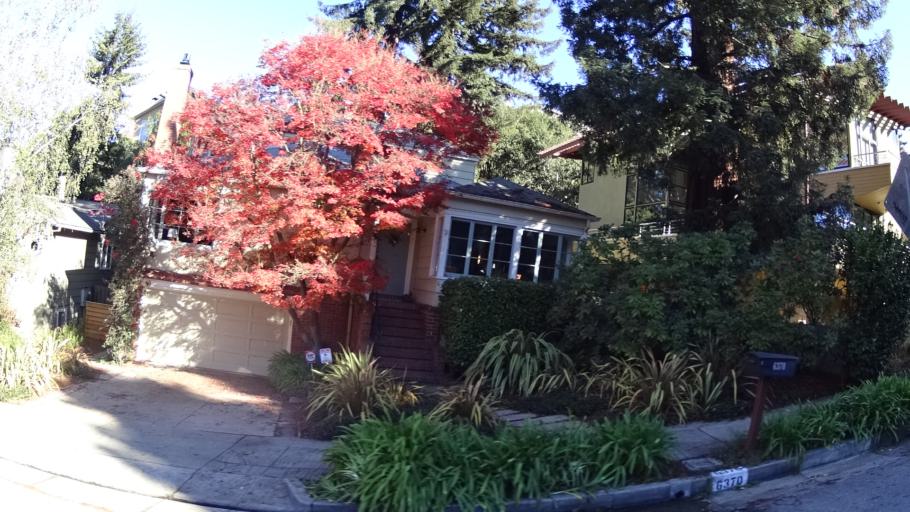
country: US
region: California
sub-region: Alameda County
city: Piedmont
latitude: 37.8467
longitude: -122.2386
